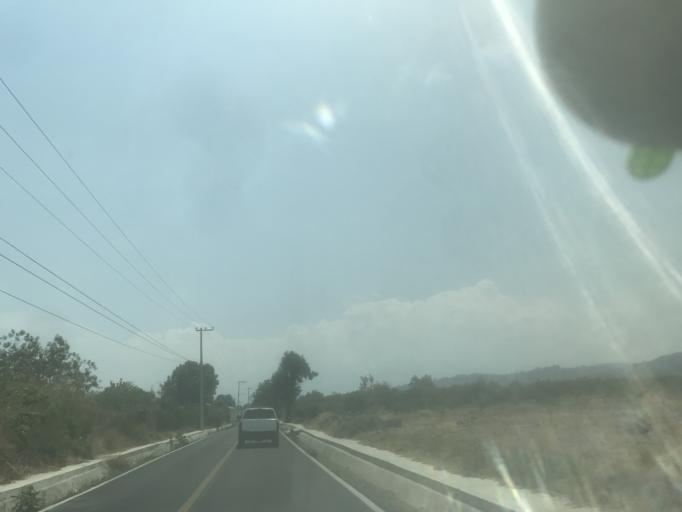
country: MX
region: Mexico
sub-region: Atlautla
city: San Andres Tlalamac
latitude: 18.9641
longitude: -98.8223
